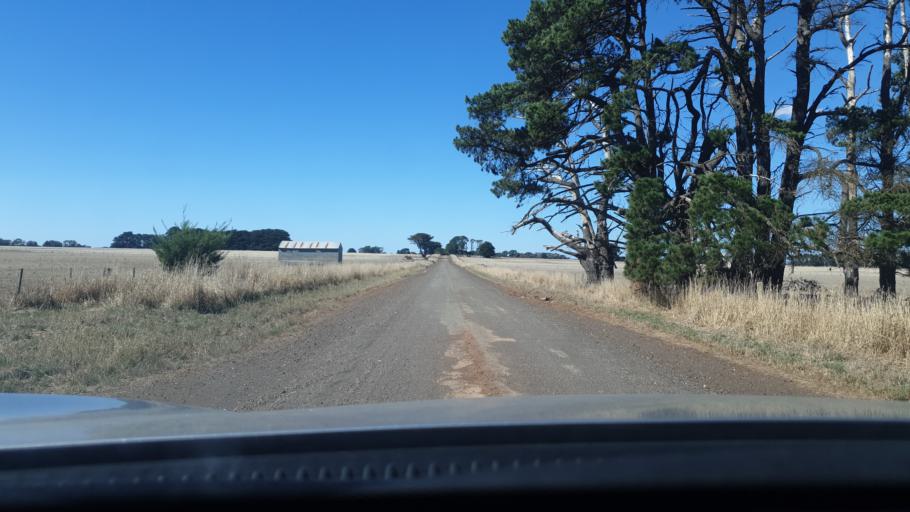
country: AU
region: Victoria
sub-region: Warrnambool
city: Warrnambool
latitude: -38.1650
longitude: 142.3787
